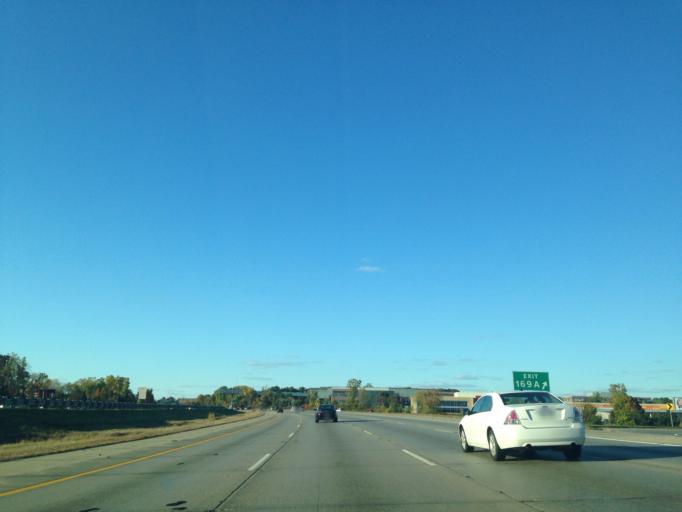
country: US
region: Michigan
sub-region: Wayne County
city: Northville
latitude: 42.4255
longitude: -83.4243
